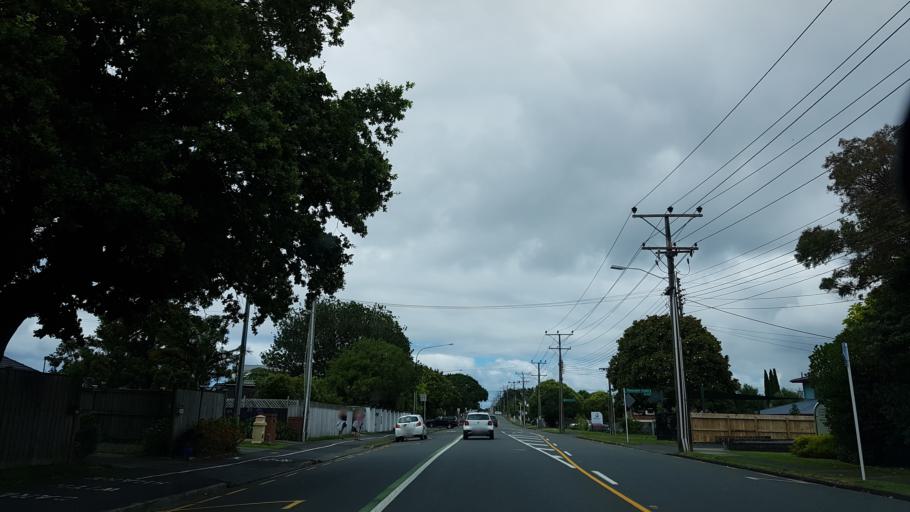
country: NZ
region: Auckland
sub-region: Auckland
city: North Shore
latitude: -36.7750
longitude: 174.7607
